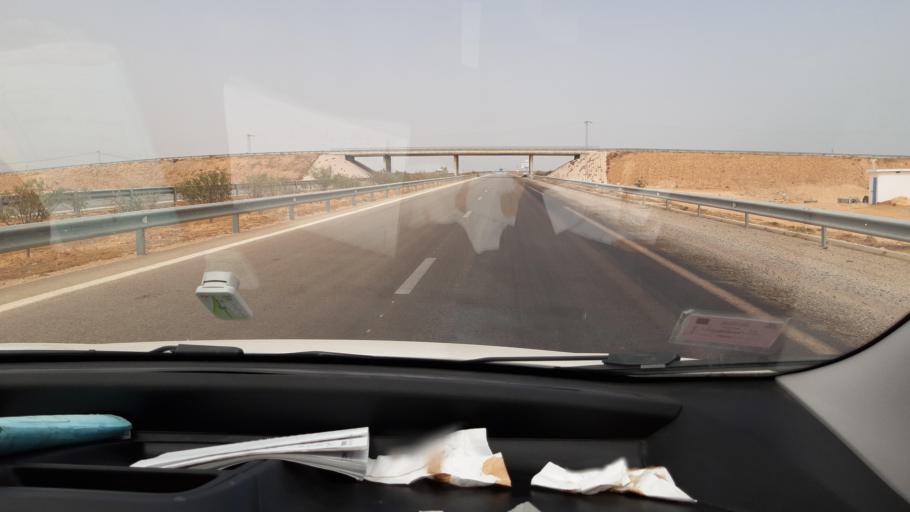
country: TN
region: Safaqis
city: Sfax
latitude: 34.8823
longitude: 10.7057
